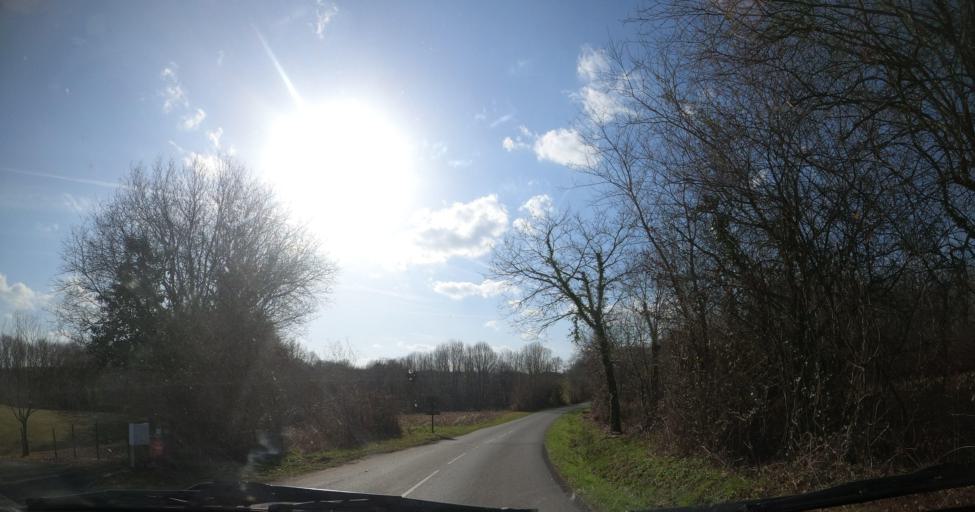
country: FR
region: Aquitaine
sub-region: Departement des Pyrenees-Atlantiques
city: Briscous
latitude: 43.4447
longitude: -1.3697
